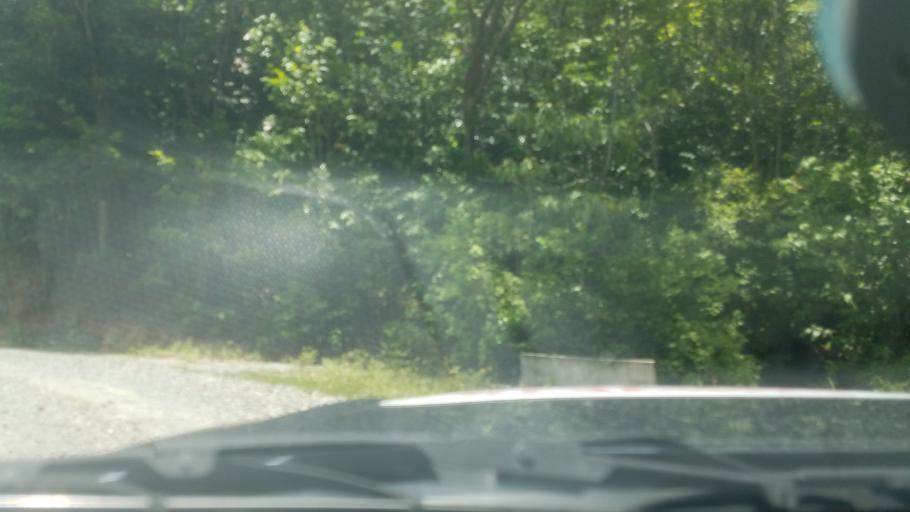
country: LC
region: Praslin
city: Praslin
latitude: 13.8674
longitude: -60.9062
